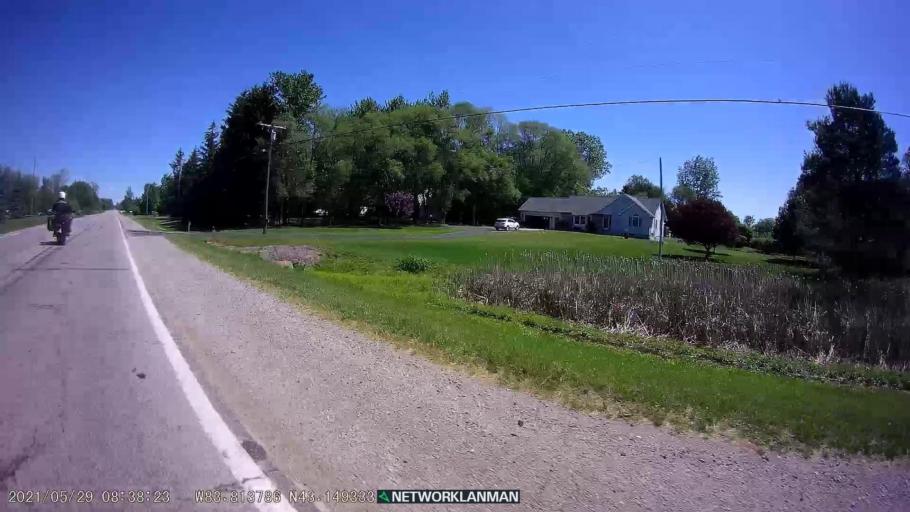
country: US
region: Michigan
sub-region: Genesee County
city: Montrose
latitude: 43.1495
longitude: -83.8138
